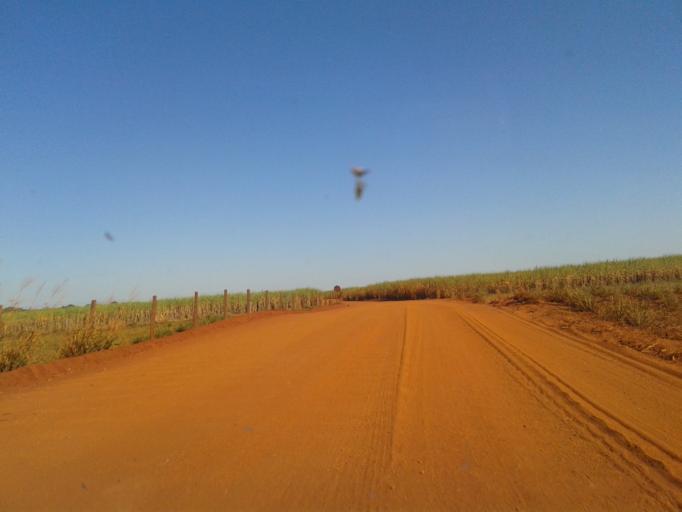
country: BR
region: Minas Gerais
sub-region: Santa Vitoria
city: Santa Vitoria
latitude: -18.8548
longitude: -50.0527
